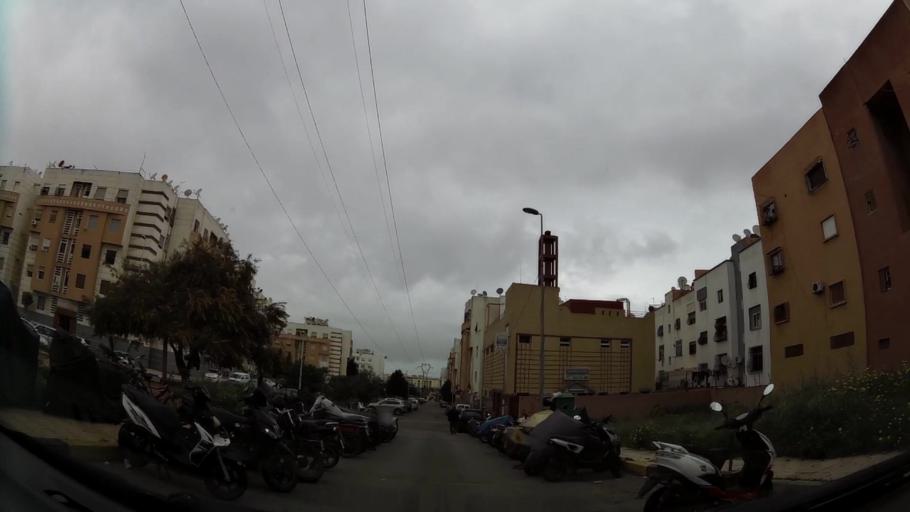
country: MA
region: Grand Casablanca
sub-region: Casablanca
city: Casablanca
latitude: 33.5318
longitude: -7.6106
